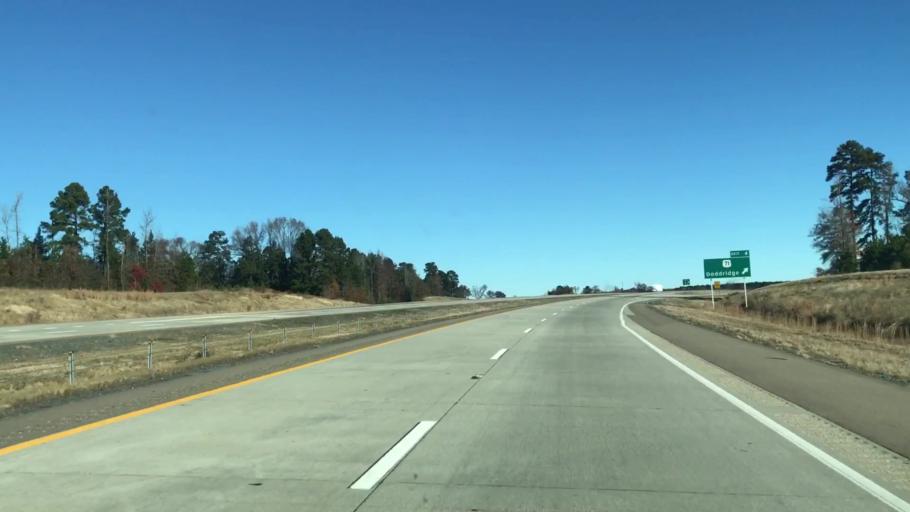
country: US
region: Louisiana
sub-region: Caddo Parish
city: Vivian
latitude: 33.0741
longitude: -93.9046
